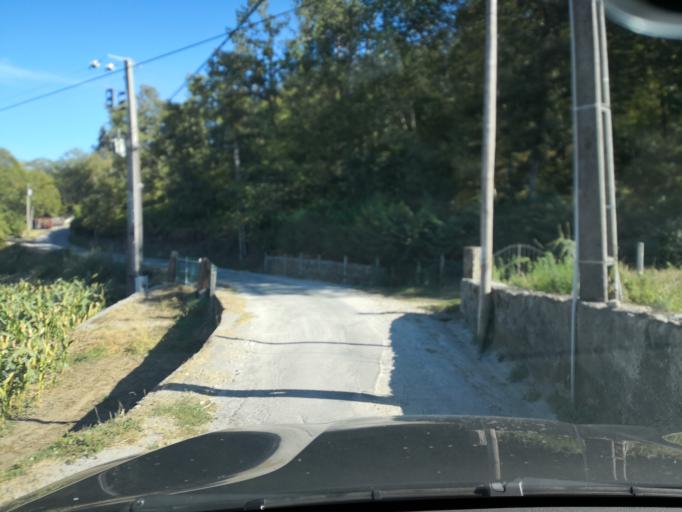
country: PT
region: Vila Real
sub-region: Santa Marta de Penaguiao
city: Santa Marta de Penaguiao
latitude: 41.2826
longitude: -7.8683
